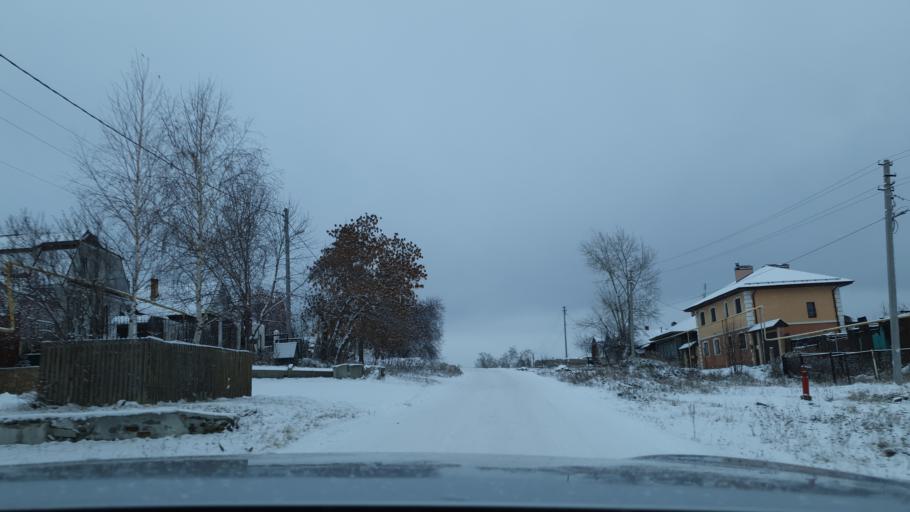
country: RU
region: Sverdlovsk
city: Istok
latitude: 56.7453
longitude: 60.6967
